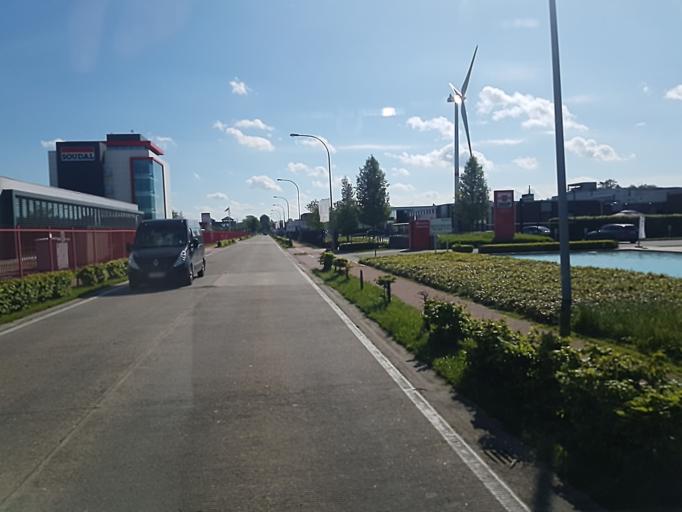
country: BE
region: Flanders
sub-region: Provincie Antwerpen
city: Turnhout
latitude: 51.2999
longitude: 4.9372
